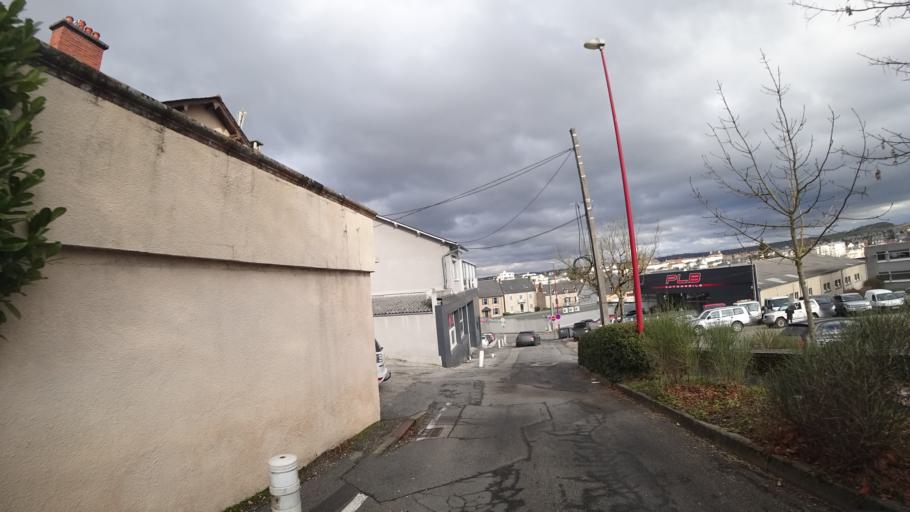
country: FR
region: Midi-Pyrenees
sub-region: Departement de l'Aveyron
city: Rodez
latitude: 44.3601
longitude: 2.5861
